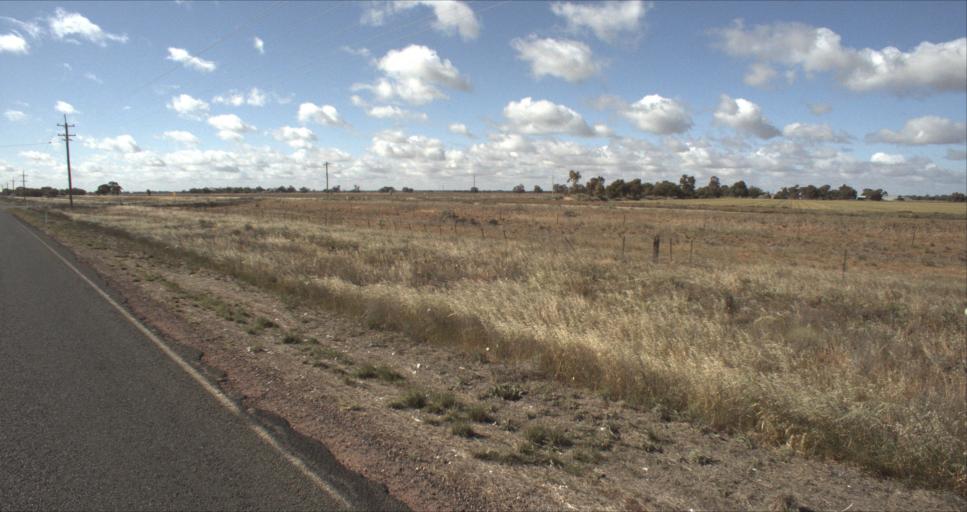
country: AU
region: New South Wales
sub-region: Leeton
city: Leeton
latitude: -34.5491
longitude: 146.2666
